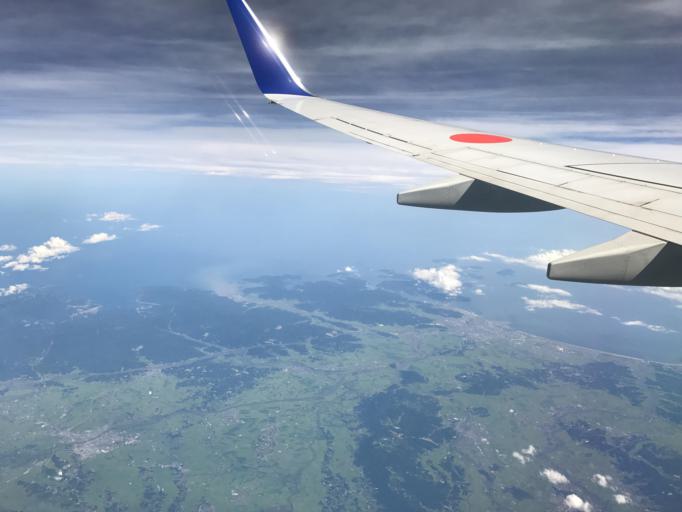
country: JP
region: Miyagi
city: Furukawa
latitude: 38.6963
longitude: 140.9071
